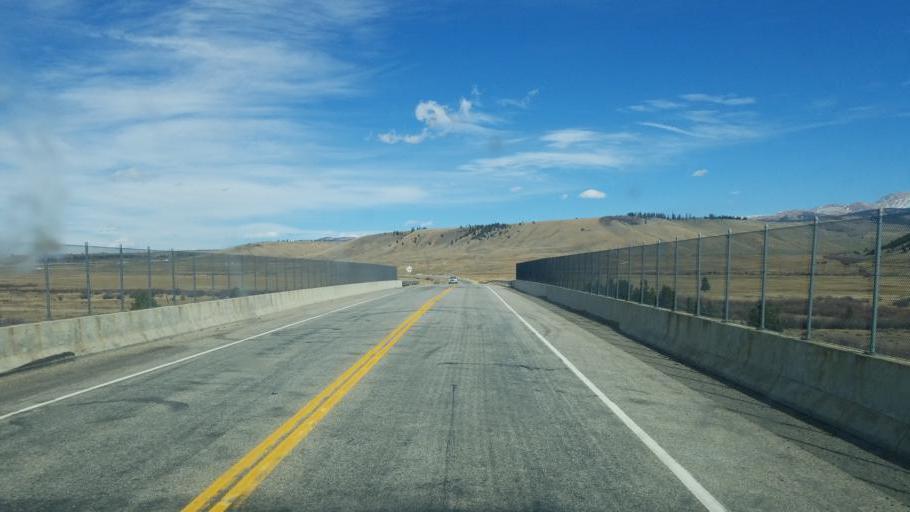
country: US
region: Colorado
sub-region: Lake County
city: Leadville
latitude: 39.1659
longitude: -106.3256
